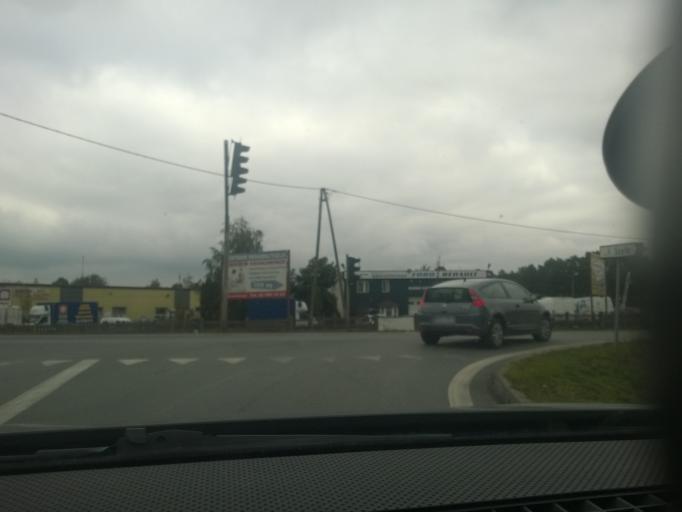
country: PL
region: Greater Poland Voivodeship
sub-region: Powiat kaliski
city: Opatowek
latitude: 51.7362
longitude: 18.1920
